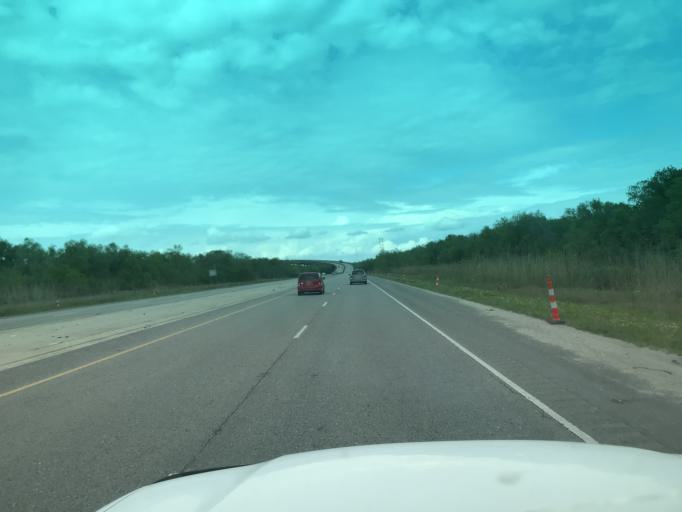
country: US
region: Louisiana
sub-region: Saint Bernard Parish
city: Chalmette
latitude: 29.9923
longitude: -89.9421
